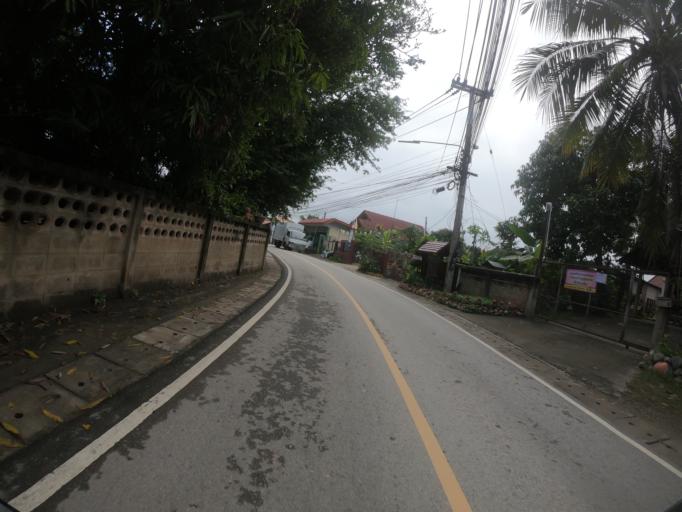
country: TH
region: Chiang Mai
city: Hang Dong
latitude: 18.7250
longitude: 98.9552
